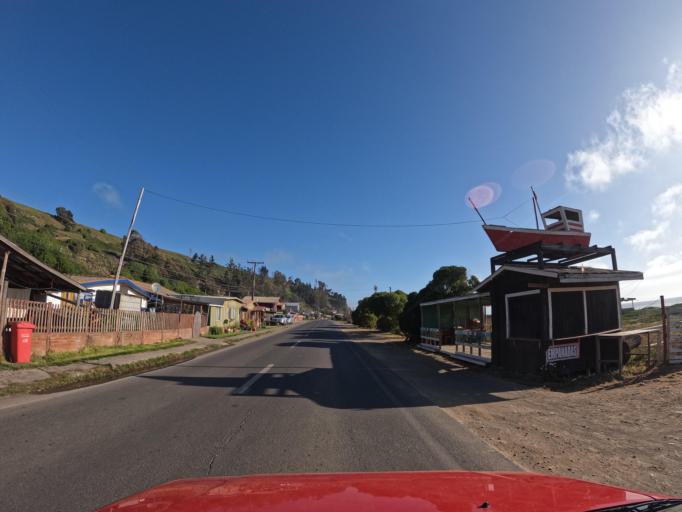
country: CL
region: Maule
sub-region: Provincia de Talca
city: Constitucion
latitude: -34.9023
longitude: -72.1797
